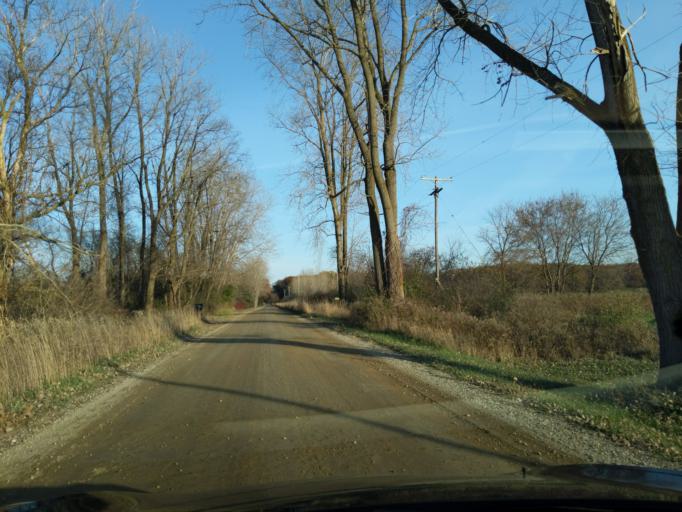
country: US
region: Michigan
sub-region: Clinton County
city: Bath
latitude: 42.7986
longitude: -84.4941
